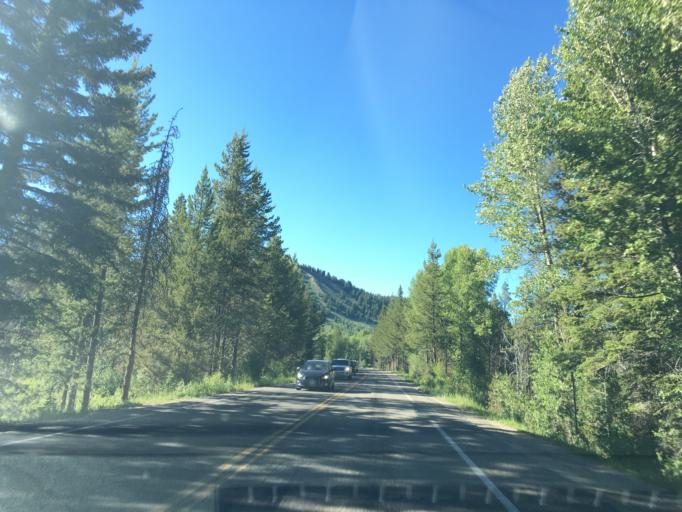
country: US
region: Wyoming
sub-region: Teton County
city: Jackson
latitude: 43.8509
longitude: -110.5178
